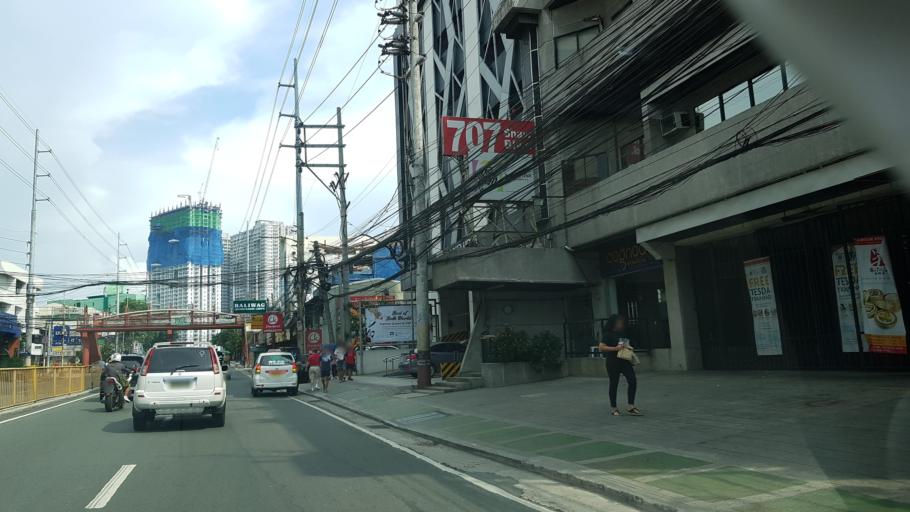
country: PH
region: Metro Manila
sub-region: Pasig
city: Pasig City
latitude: 14.5733
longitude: 121.0628
